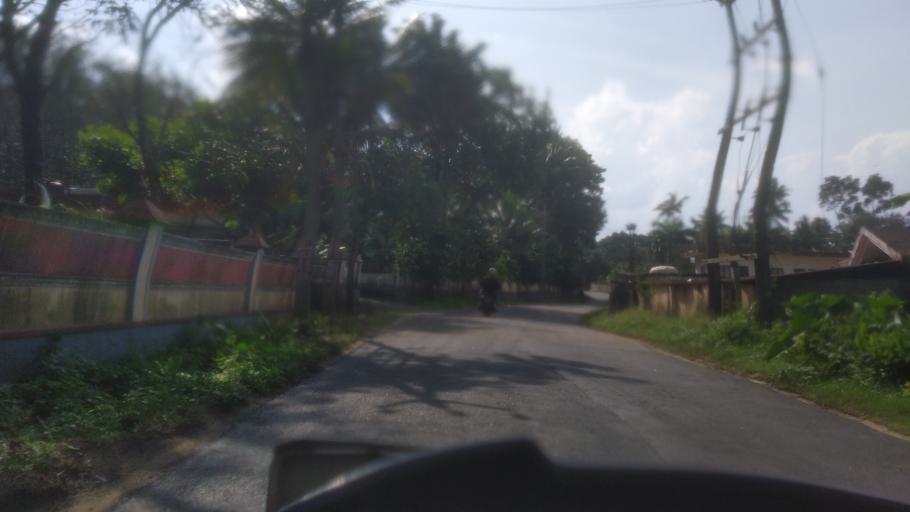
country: IN
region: Kerala
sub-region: Ernakulam
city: Kotamangalam
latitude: 10.0021
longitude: 76.7304
